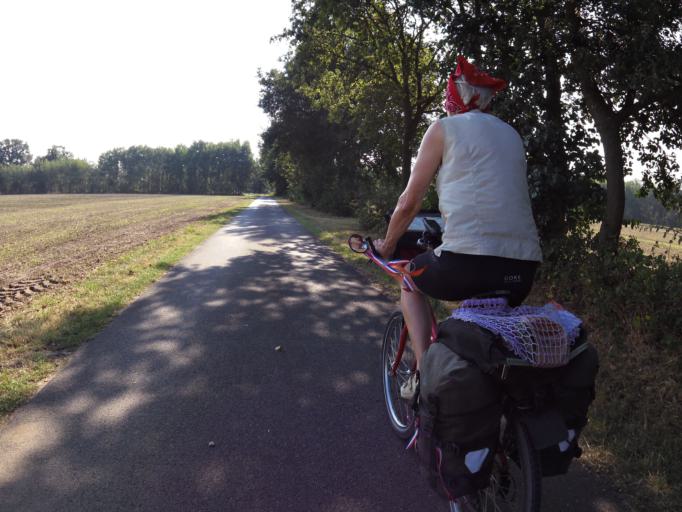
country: DE
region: North Rhine-Westphalia
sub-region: Regierungsbezirk Detmold
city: Harsewinkel
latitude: 51.9453
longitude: 8.1832
